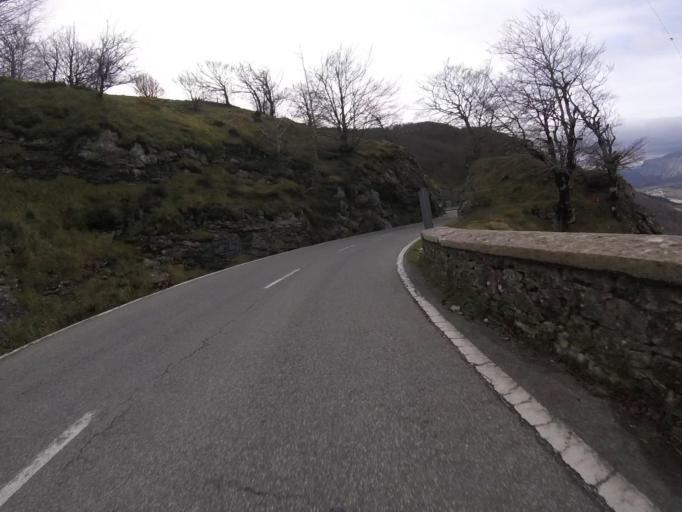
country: ES
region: Navarre
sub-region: Provincia de Navarra
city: Olazagutia
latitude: 42.8596
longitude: -2.1818
